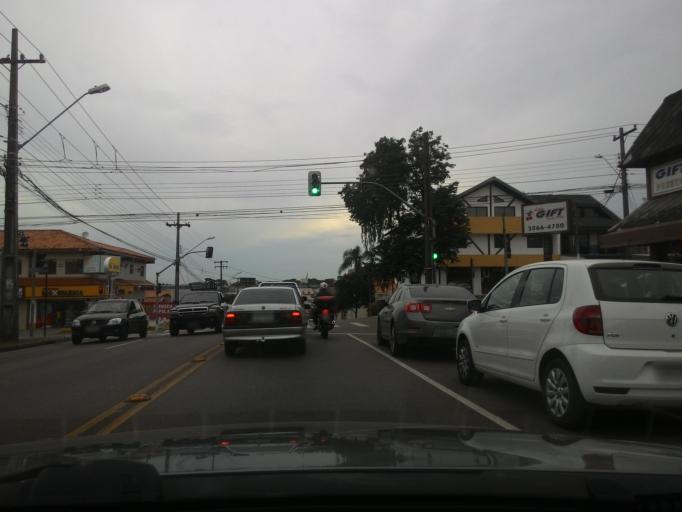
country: BR
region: Parana
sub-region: Pinhais
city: Pinhais
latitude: -25.4454
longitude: -49.2235
